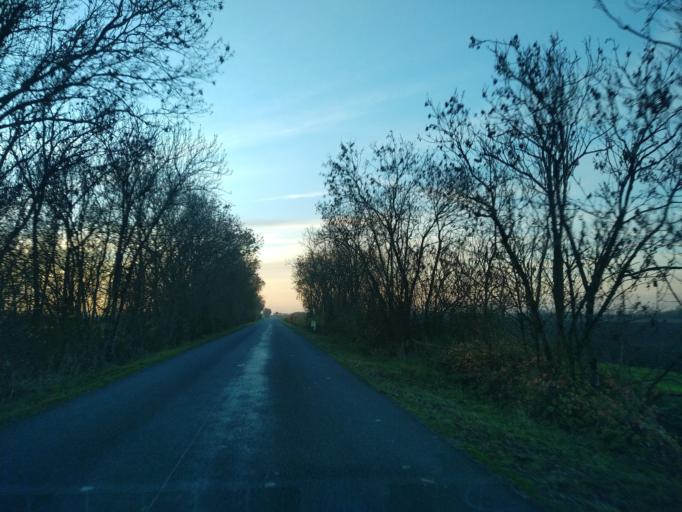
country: FR
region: Pays de la Loire
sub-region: Departement de la Vendee
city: Maillezais
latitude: 46.3785
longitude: -0.7657
